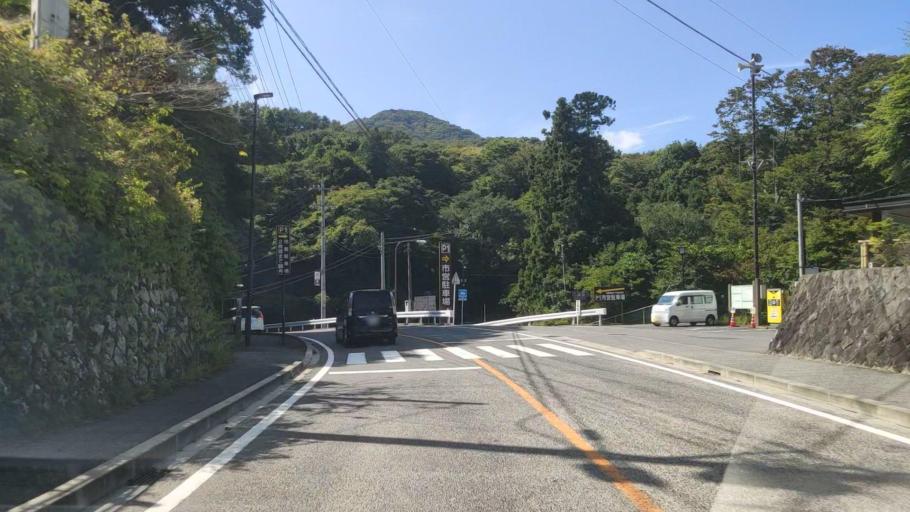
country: JP
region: Gunma
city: Shibukawa
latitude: 36.4989
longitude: 138.9157
